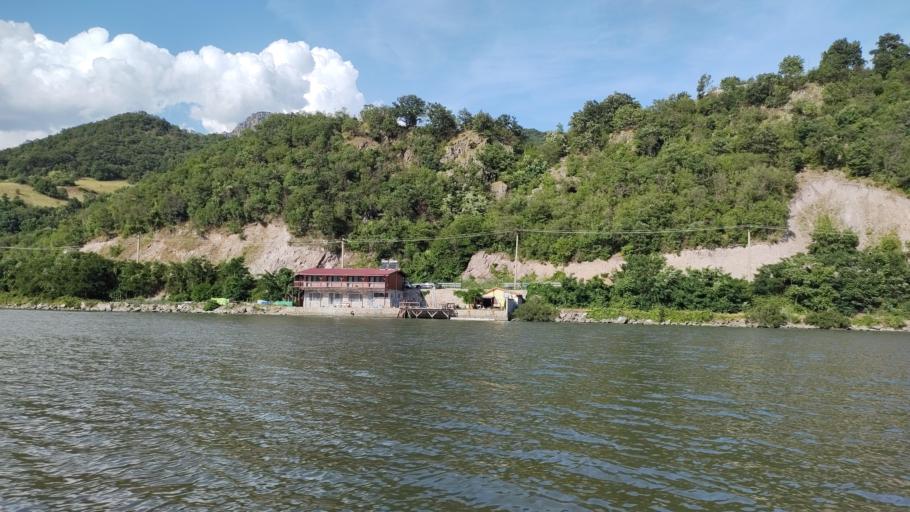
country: RO
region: Mehedinti
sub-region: Comuna Svinita
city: Svinita
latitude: 44.5508
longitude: 22.0353
